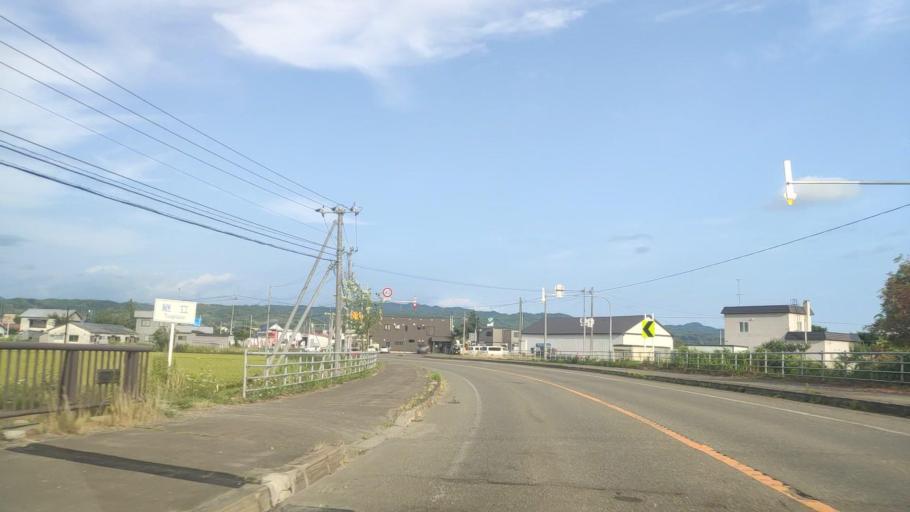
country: JP
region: Hokkaido
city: Iwamizawa
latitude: 43.0203
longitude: 141.8533
